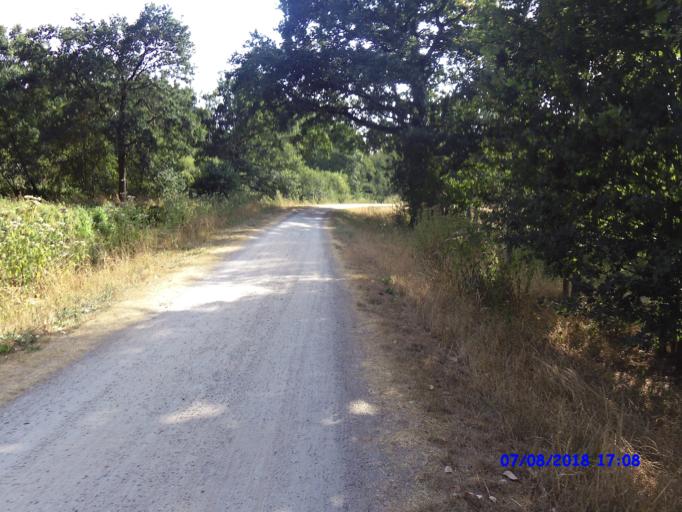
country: BE
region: Flanders
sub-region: Provincie Antwerpen
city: Westerlo
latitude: 51.0889
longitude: 4.9236
